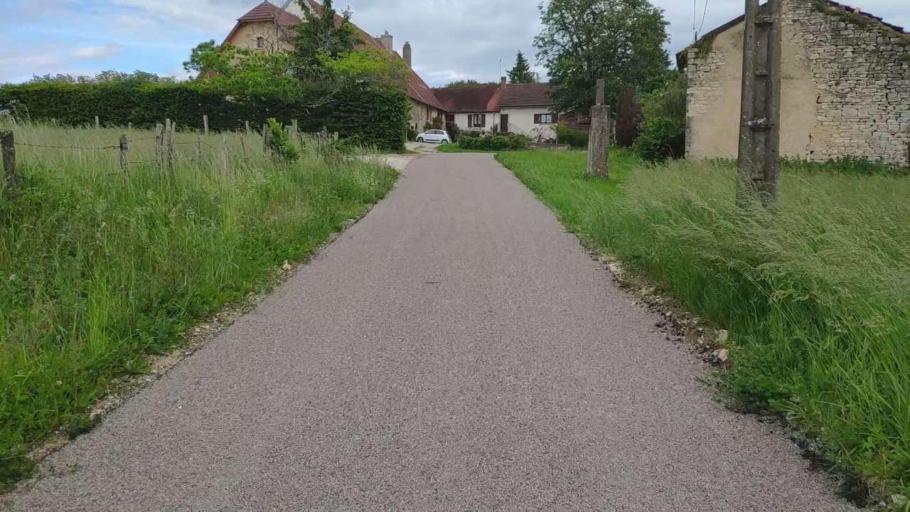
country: FR
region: Franche-Comte
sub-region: Departement du Jura
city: Bletterans
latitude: 46.7974
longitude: 5.5464
